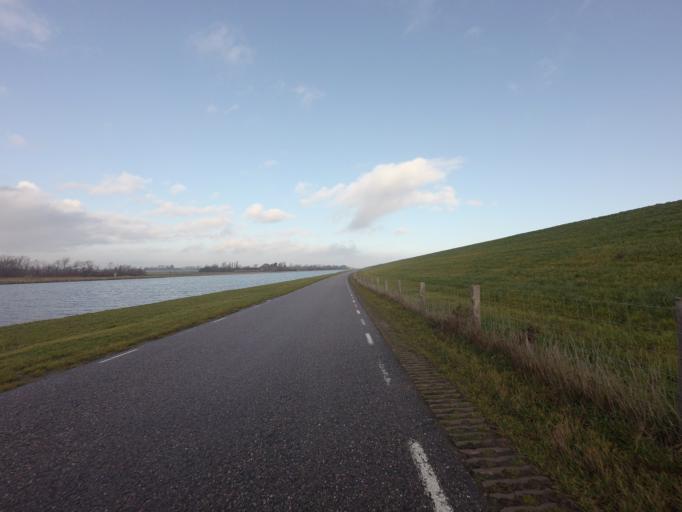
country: NL
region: North Holland
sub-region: Gemeente Texel
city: Den Burg
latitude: 53.1044
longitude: 4.8979
